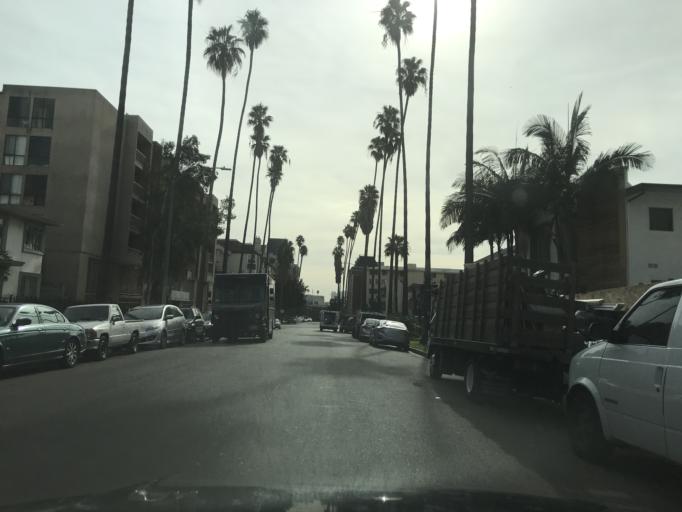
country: US
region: California
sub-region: Los Angeles County
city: Hollywood
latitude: 34.0645
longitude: -118.3129
